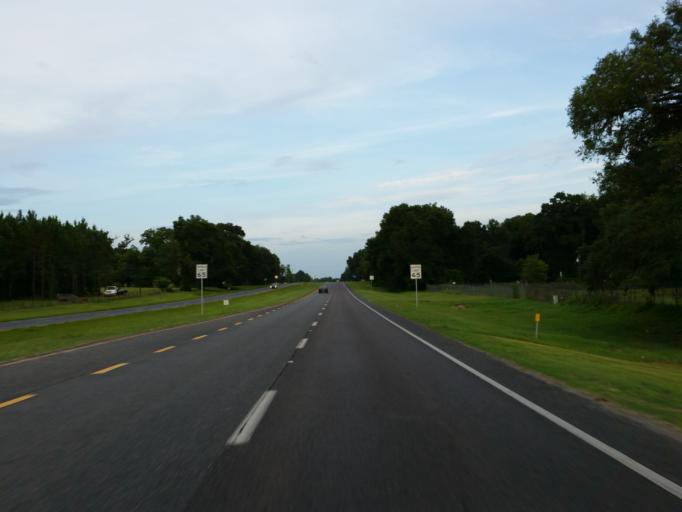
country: US
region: Florida
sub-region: Alachua County
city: High Springs
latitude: 29.8178
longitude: -82.5760
